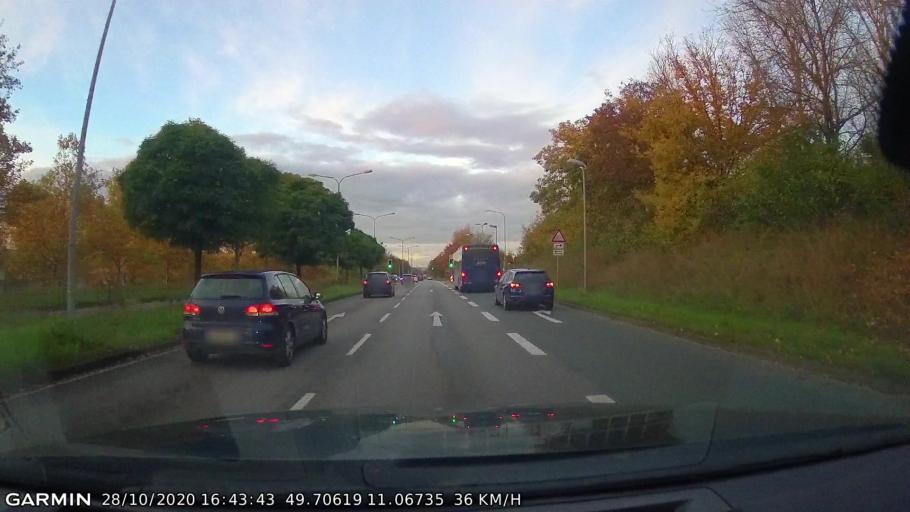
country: DE
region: Bavaria
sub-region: Upper Franconia
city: Forchheim
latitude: 49.7063
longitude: 11.0674
